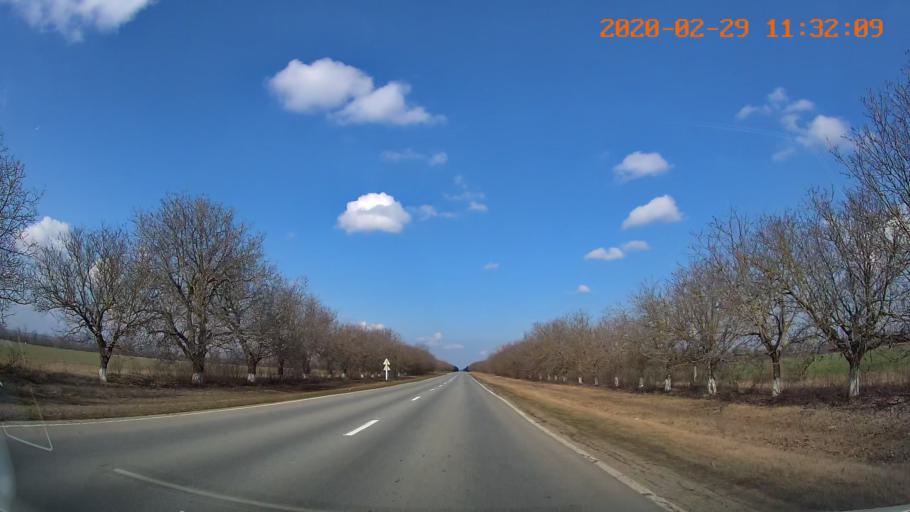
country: MD
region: Rezina
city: Saharna
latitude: 47.5339
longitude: 29.0974
